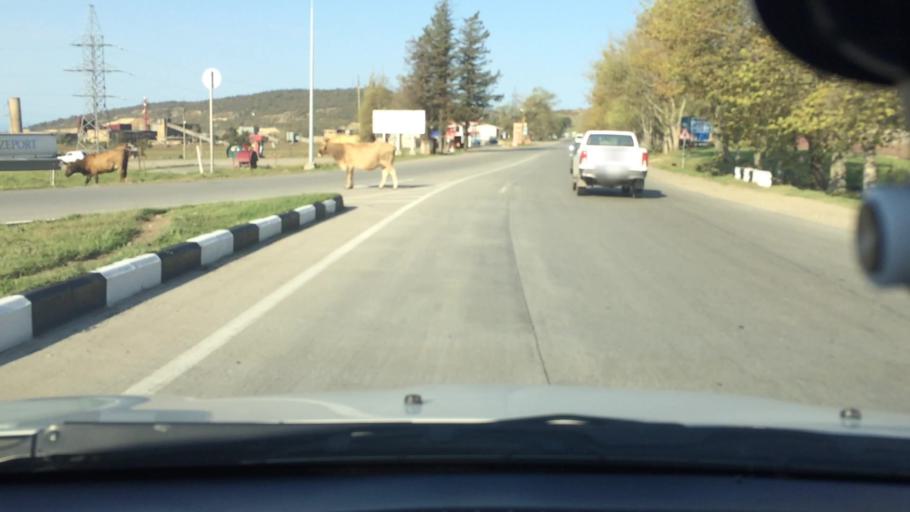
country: GE
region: Imereti
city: Kutaisi
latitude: 42.2138
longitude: 42.8191
